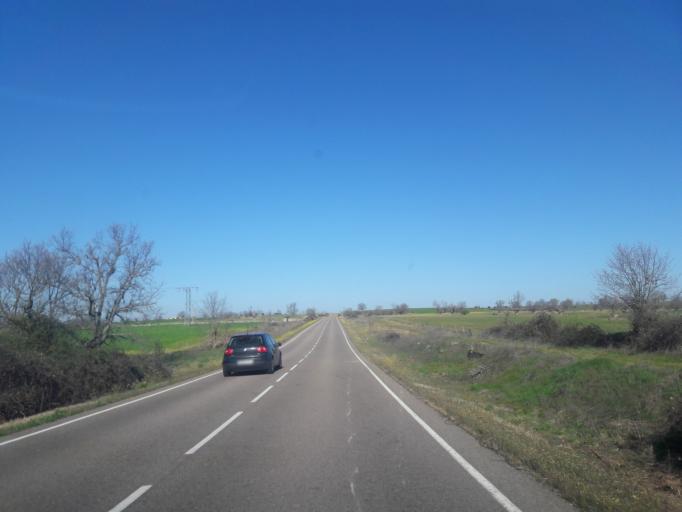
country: ES
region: Castille and Leon
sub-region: Provincia de Salamanca
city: Valderrodrigo
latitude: 41.0705
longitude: -6.5213
